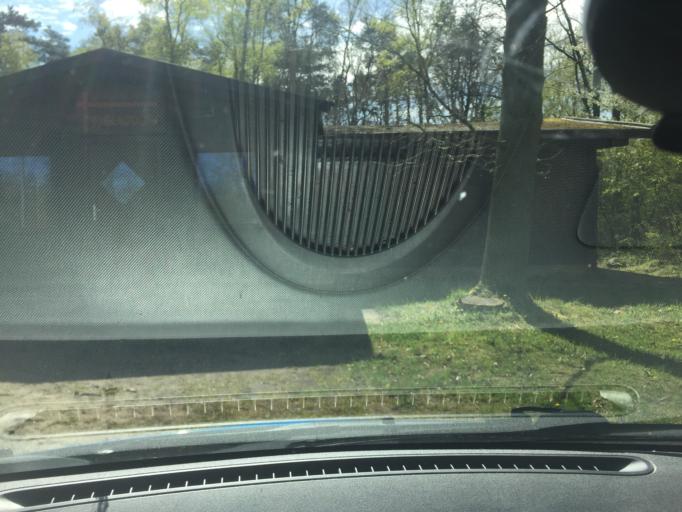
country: DE
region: Lower Saxony
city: Emmendorf
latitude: 52.9970
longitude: 10.5980
